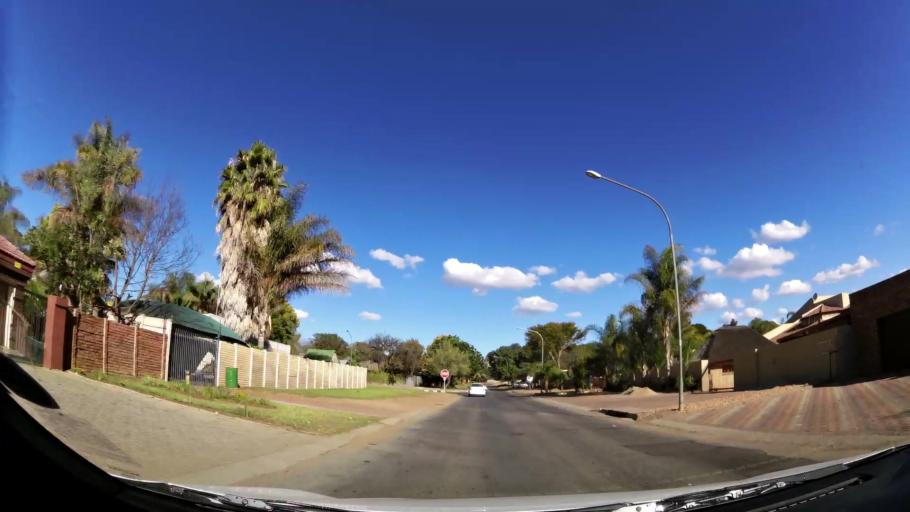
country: ZA
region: Limpopo
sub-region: Capricorn District Municipality
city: Polokwane
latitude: -23.9131
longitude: 29.4819
